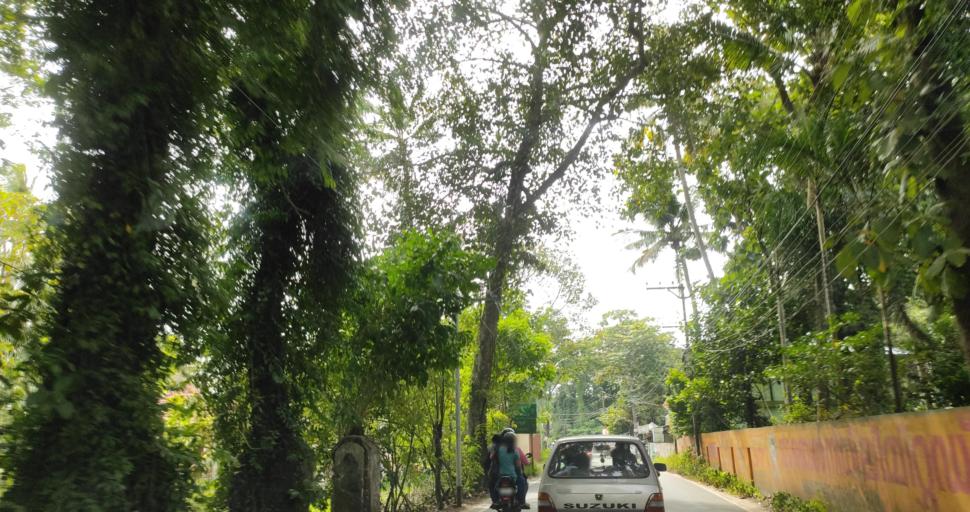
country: IN
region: Kerala
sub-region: Alappuzha
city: Shertallai
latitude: 9.6845
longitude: 76.3526
